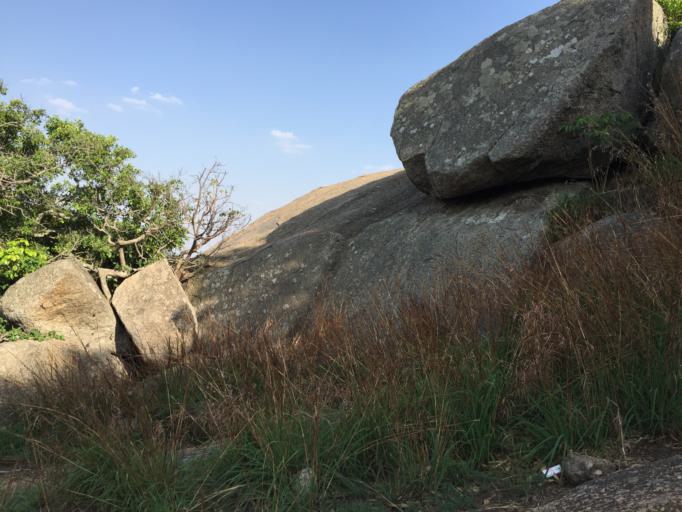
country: IN
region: Karnataka
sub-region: Ramanagara
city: Magadi
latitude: 12.9206
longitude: 77.2929
